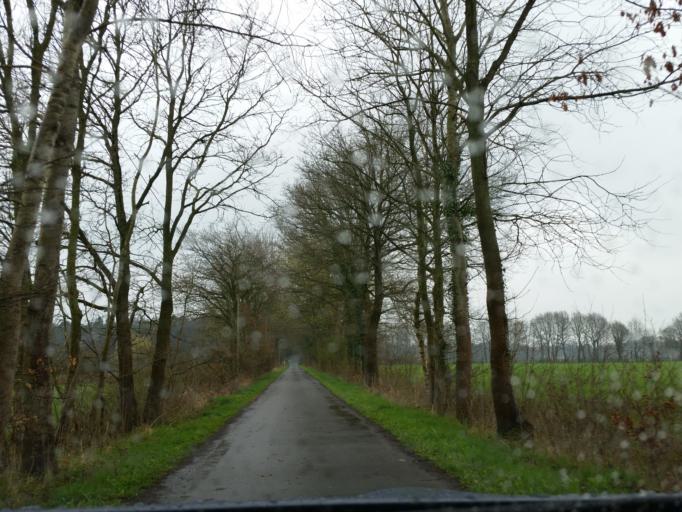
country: DE
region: Lower Saxony
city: Hipstedt
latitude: 53.4751
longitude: 8.9645
